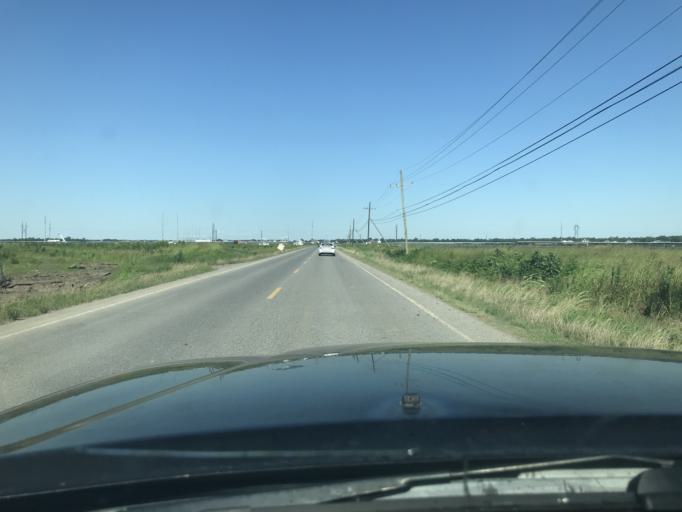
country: US
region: Louisiana
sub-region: West Baton Rouge Parish
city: Brusly
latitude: 30.4688
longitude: -91.3195
